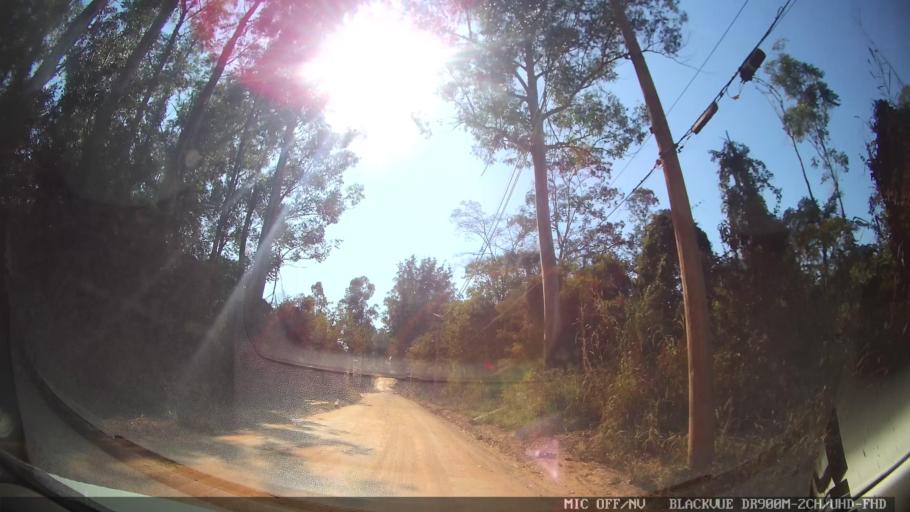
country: BR
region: Sao Paulo
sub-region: Itupeva
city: Itupeva
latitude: -23.1212
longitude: -47.0445
